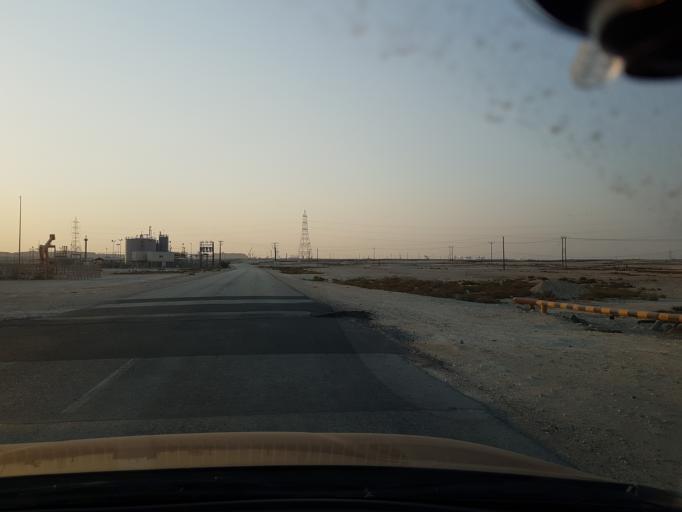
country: BH
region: Central Governorate
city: Dar Kulayb
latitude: 26.0156
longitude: 50.5769
